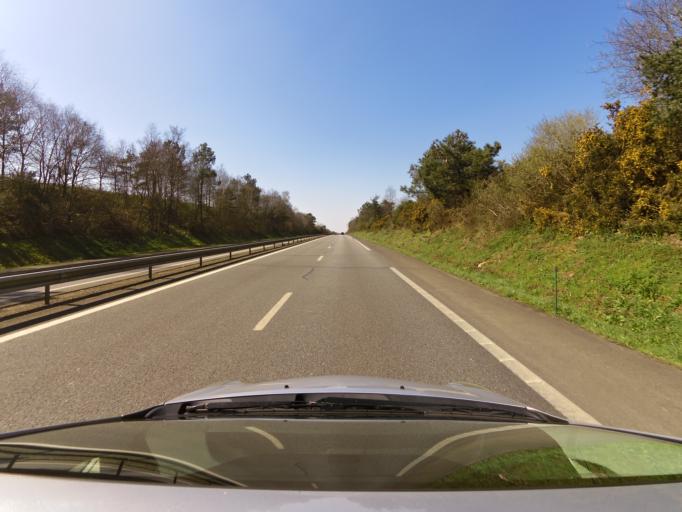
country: FR
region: Brittany
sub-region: Departement du Morbihan
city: Bignan
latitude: 47.9137
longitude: -2.7458
